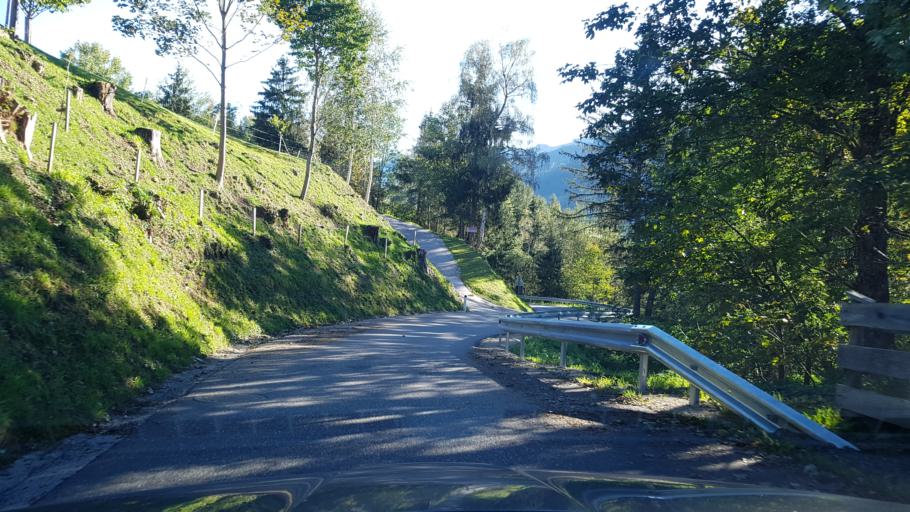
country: AT
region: Styria
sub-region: Politischer Bezirk Liezen
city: Grobming
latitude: 47.4434
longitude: 13.9359
